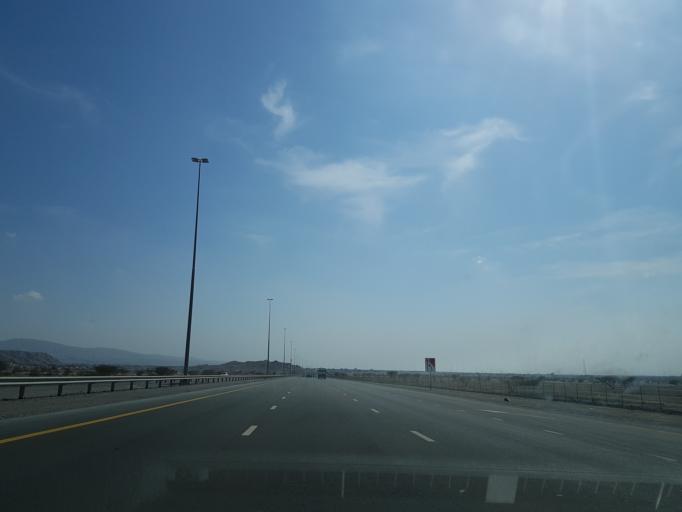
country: AE
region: Ra's al Khaymah
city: Ras al-Khaimah
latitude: 25.7434
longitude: 56.0157
